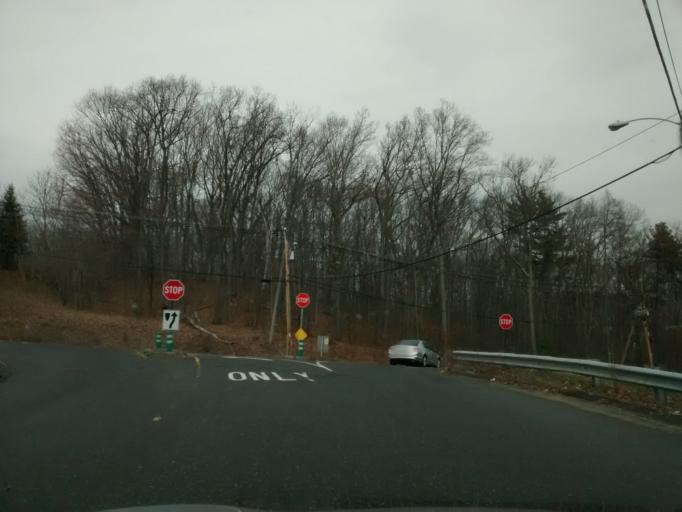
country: US
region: Massachusetts
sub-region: Worcester County
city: Hamilton
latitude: 42.2893
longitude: -71.7605
